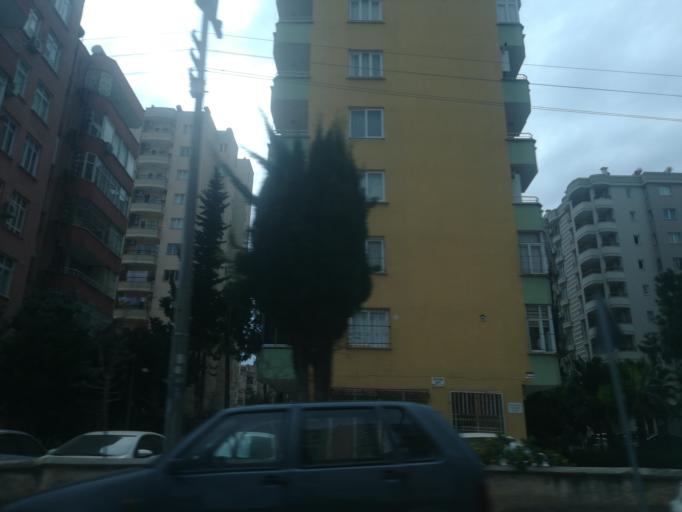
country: TR
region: Adana
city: Adana
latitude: 37.0457
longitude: 35.2902
